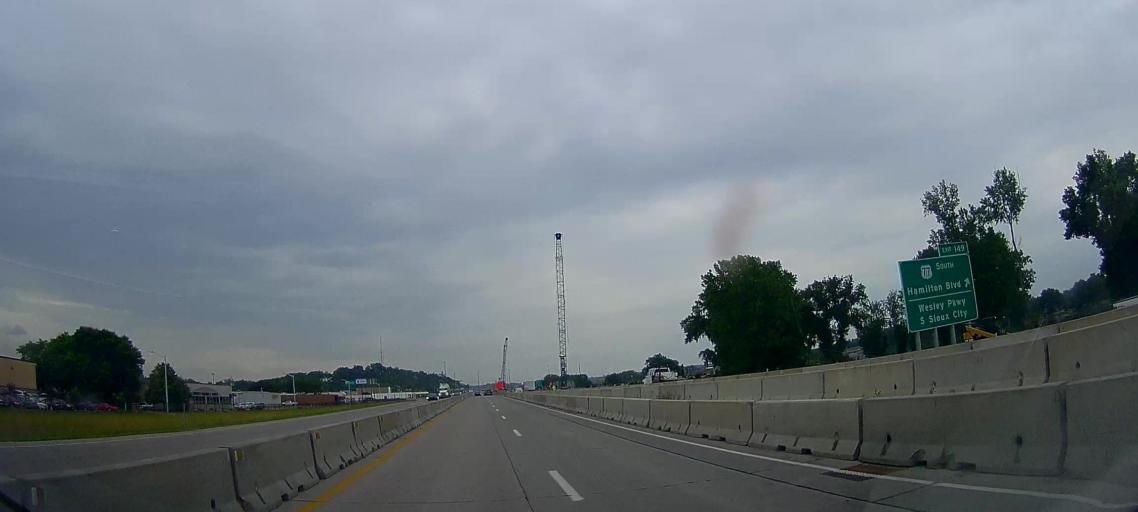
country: US
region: Nebraska
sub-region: Dakota County
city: South Sioux City
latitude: 42.4918
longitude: -96.4305
